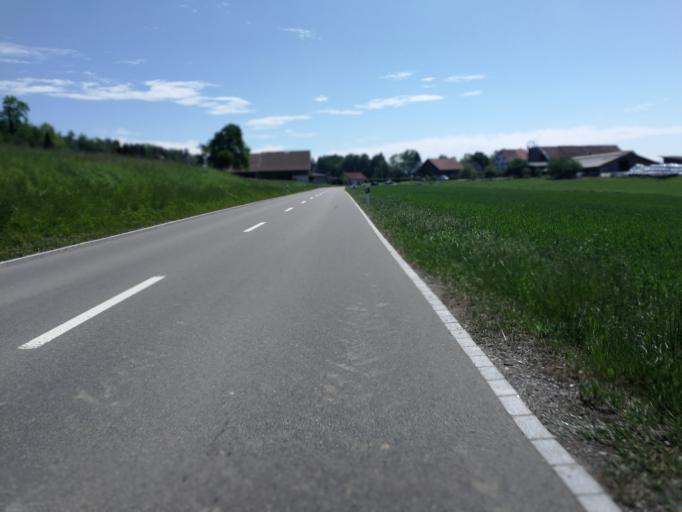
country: CH
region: Zurich
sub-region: Bezirk Uster
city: Aesch
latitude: 47.3073
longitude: 8.6386
